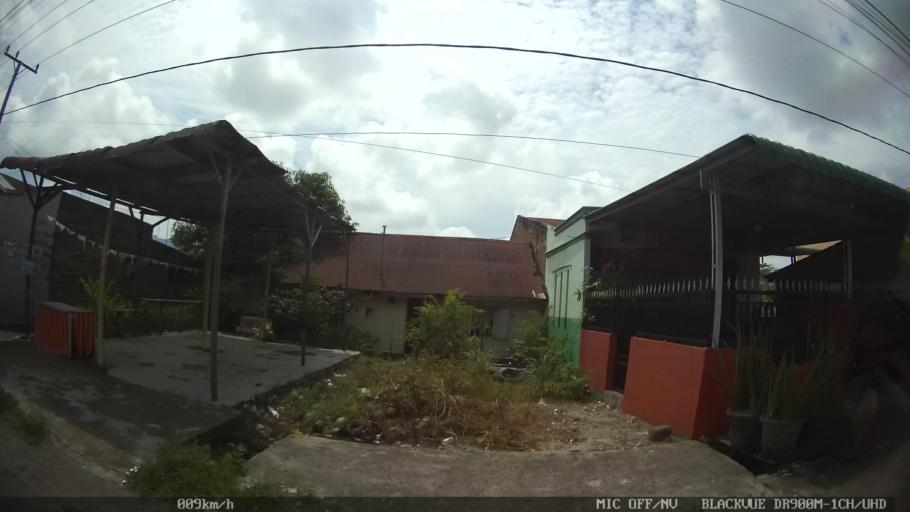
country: ID
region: North Sumatra
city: Percut
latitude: 3.6179
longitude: 98.7645
